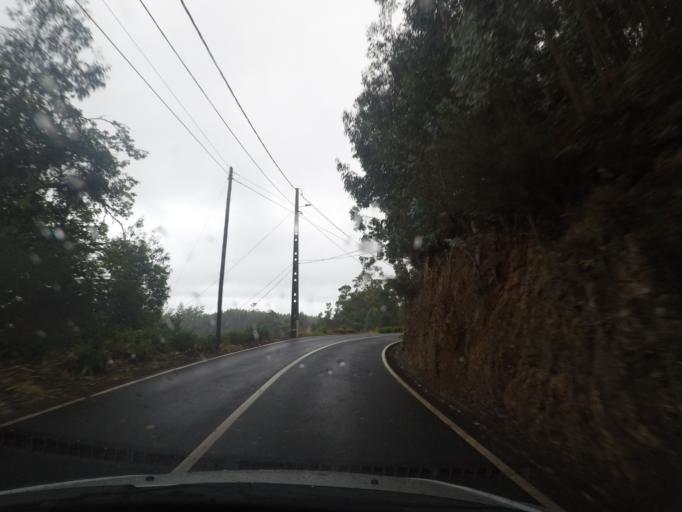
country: PT
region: Madeira
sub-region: Santa Cruz
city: Camacha
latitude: 32.6963
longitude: -16.8385
